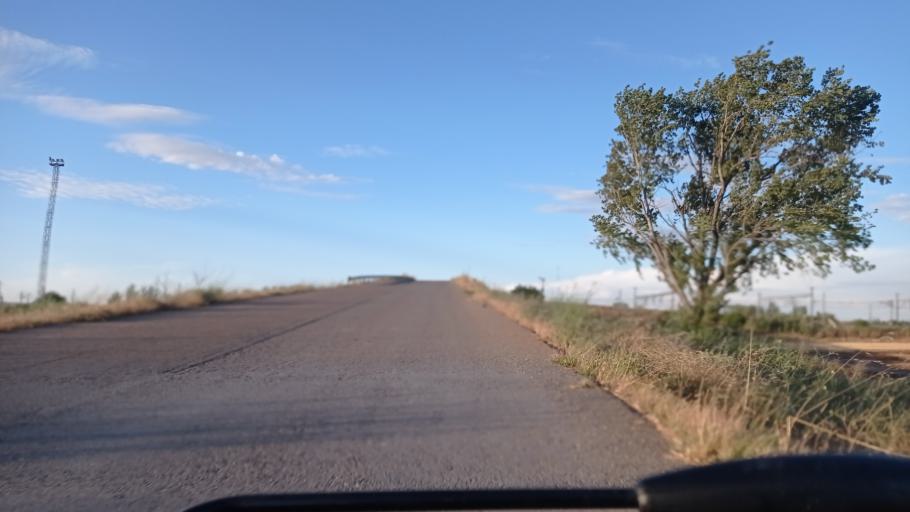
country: ES
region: Aragon
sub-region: Provincia de Zaragoza
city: Oliver-Valdefierro, Oliver, Valdefierro
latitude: 41.6743
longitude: -0.9414
